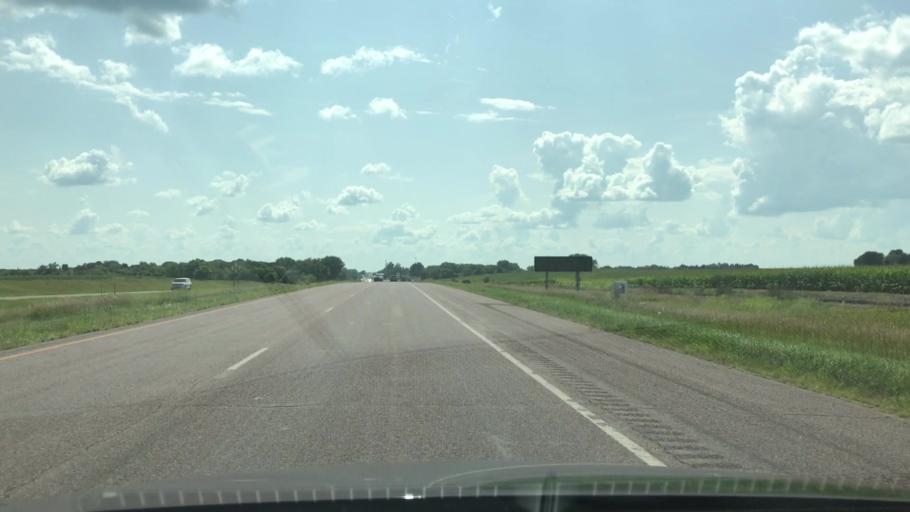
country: US
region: Minnesota
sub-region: Blue Earth County
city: Lake Crystal
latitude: 44.1223
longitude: -94.1970
